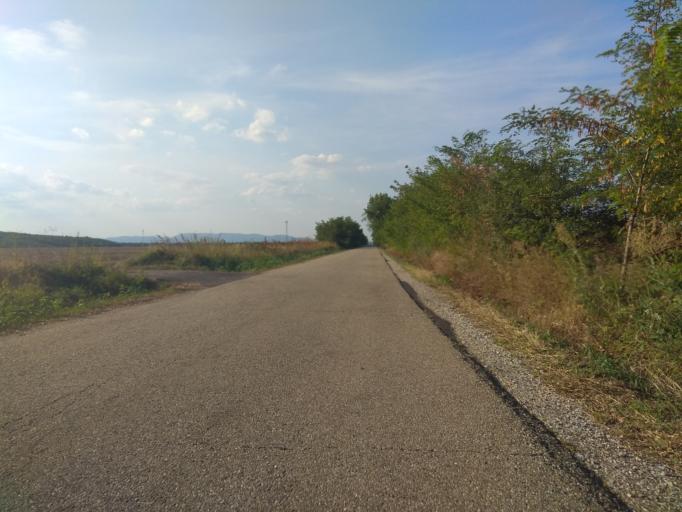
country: HU
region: Borsod-Abauj-Zemplen
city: Harsany
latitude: 47.9091
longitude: 20.7427
